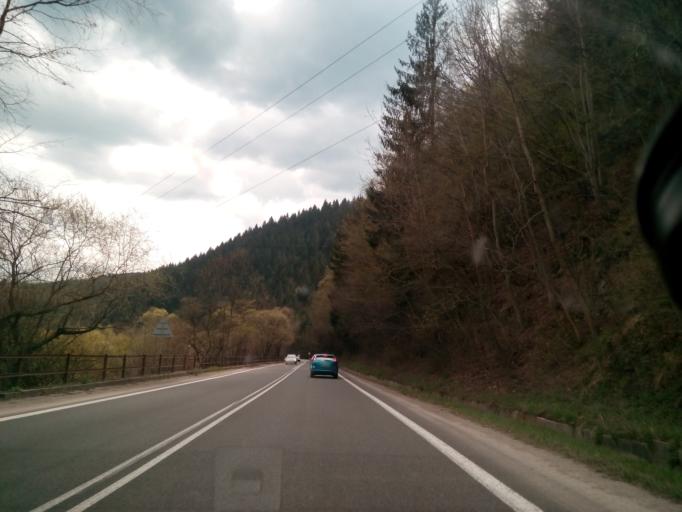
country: SK
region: Zilinsky
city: Ruzomberok
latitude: 49.1139
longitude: 19.2243
